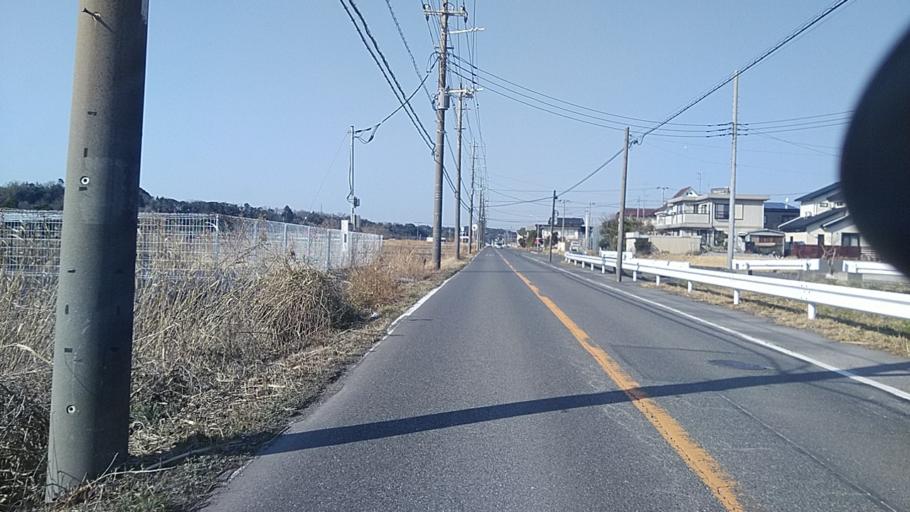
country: JP
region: Chiba
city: Mobara
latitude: 35.4509
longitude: 140.2923
